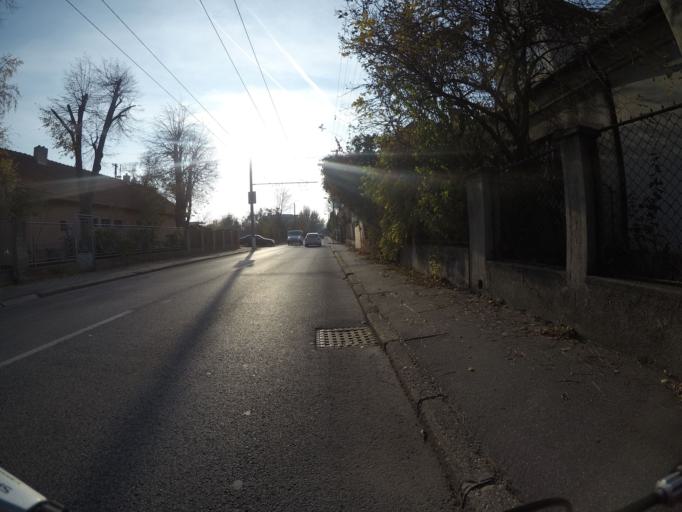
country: SK
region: Bratislavsky
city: Bratislava
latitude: 48.1696
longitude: 17.1642
